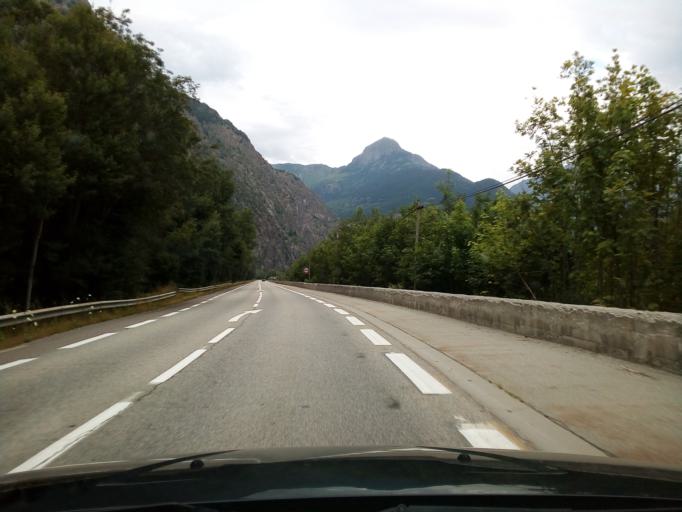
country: FR
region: Rhone-Alpes
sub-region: Departement de l'Isere
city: Huez
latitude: 45.0512
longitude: 6.0471
